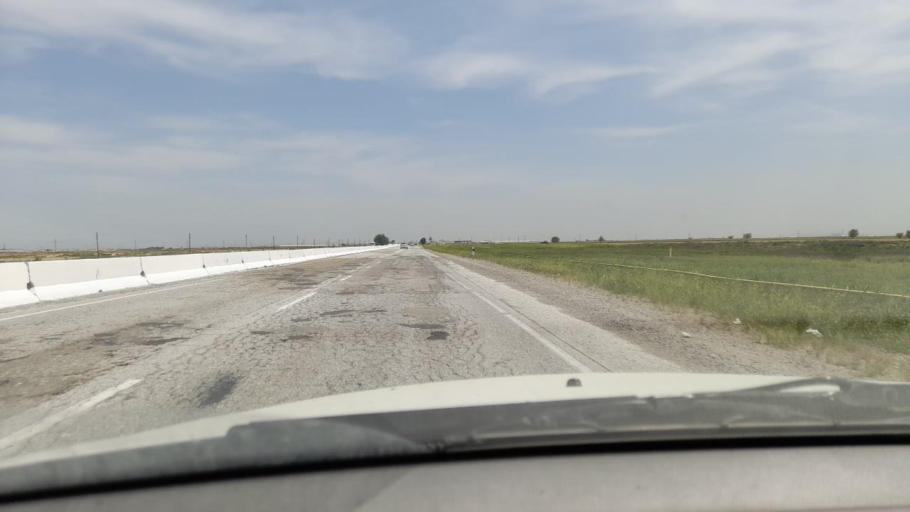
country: UZ
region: Navoiy
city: Konimex
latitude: 40.1165
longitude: 65.1121
